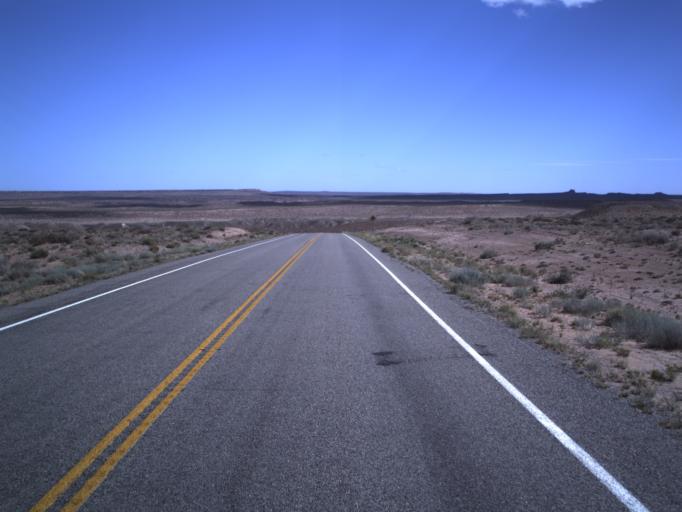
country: US
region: Utah
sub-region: Emery County
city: Ferron
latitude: 38.3365
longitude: -110.6865
